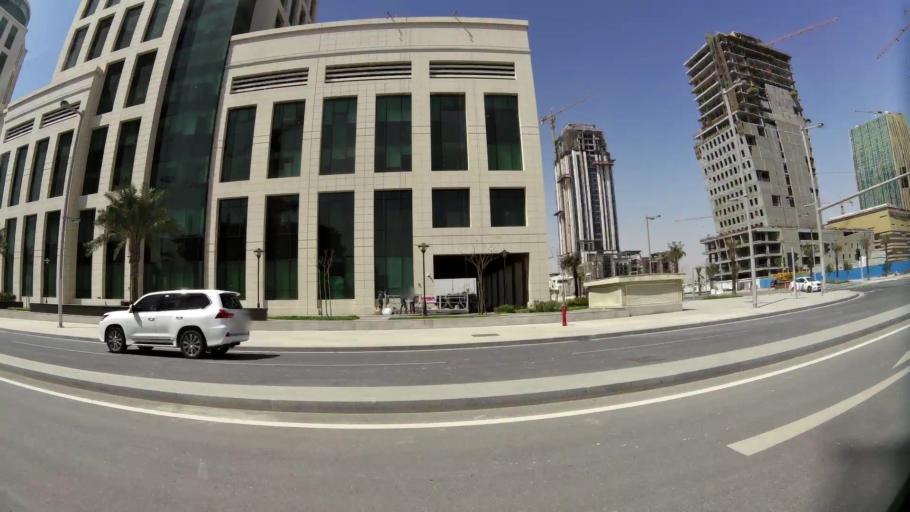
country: QA
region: Baladiyat ad Dawhah
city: Doha
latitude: 25.3943
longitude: 51.5219
